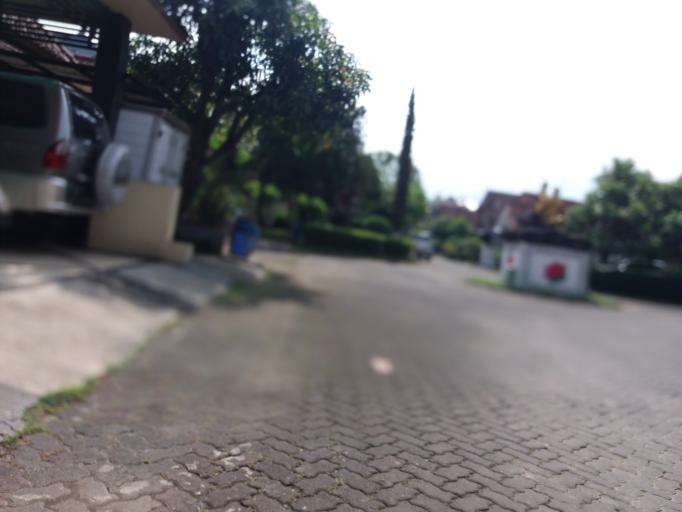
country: ID
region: West Java
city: Bandung
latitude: -6.9160
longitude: 107.6530
